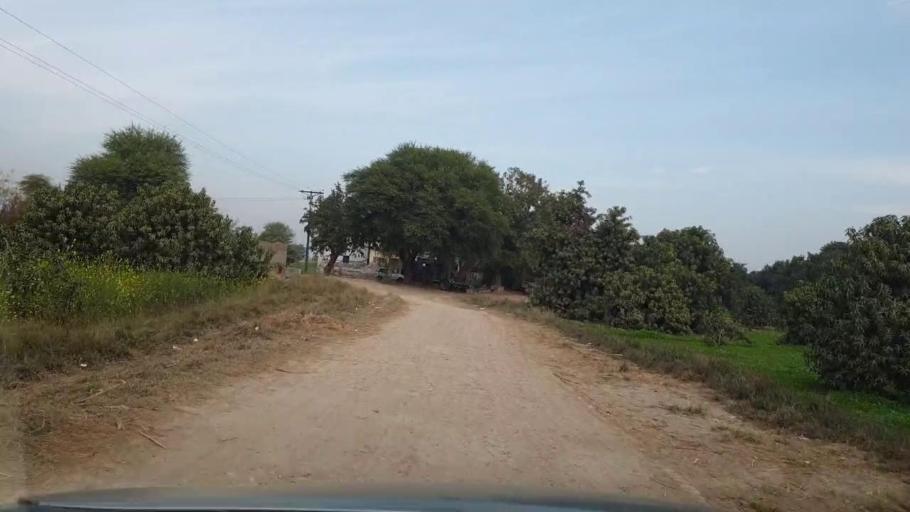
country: PK
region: Sindh
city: Matiari
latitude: 25.5639
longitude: 68.5300
